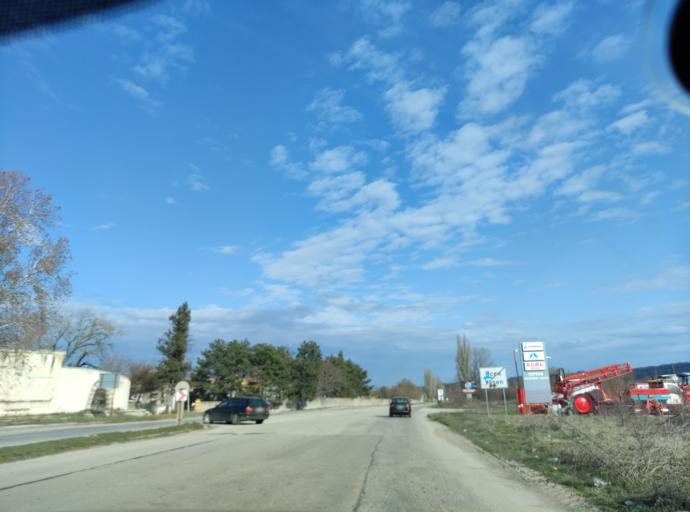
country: BG
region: Pleven
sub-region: Obshtina Dolna Mitropoliya
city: Dolna Mitropoliya
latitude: 43.4334
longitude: 24.5349
